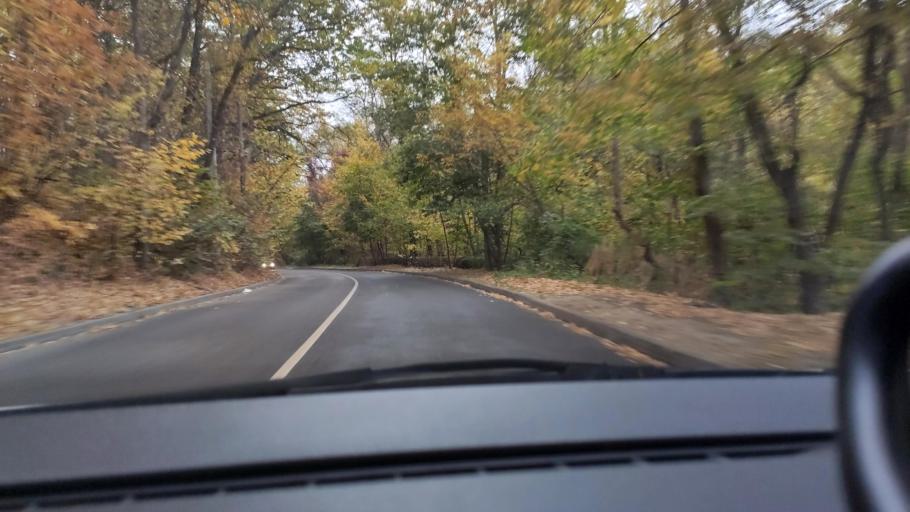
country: RU
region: Voronezj
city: Voronezh
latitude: 51.7212
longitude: 39.2356
